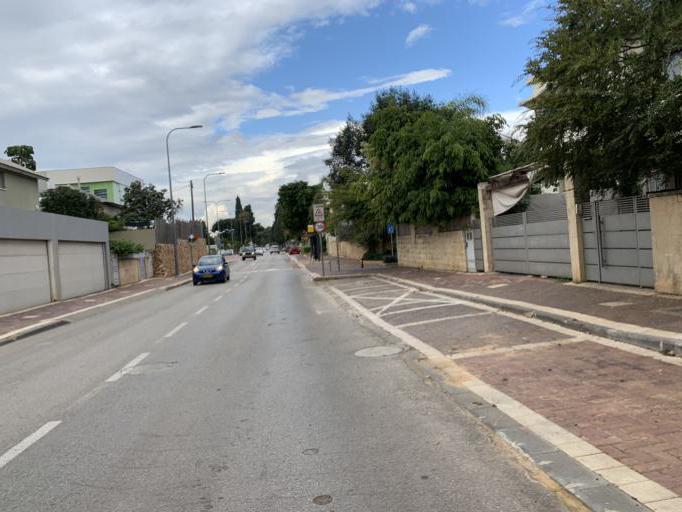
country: IL
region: Central District
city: Hod HaSharon
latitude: 32.1597
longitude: 34.8868
